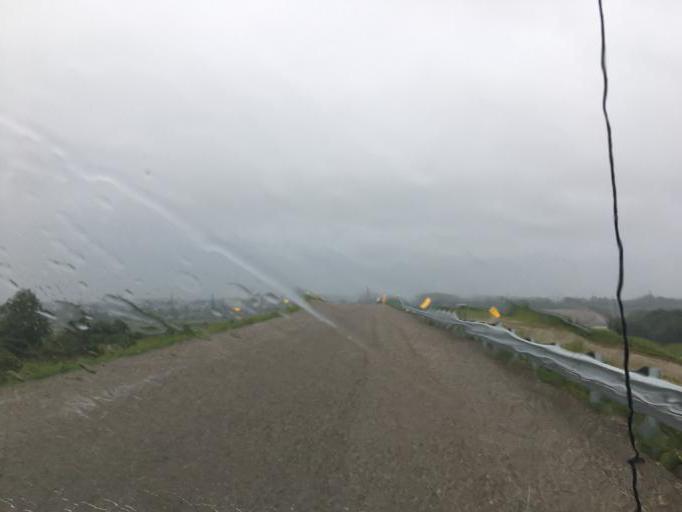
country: CA
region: Ontario
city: Kitchener
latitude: 43.4358
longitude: -80.5707
